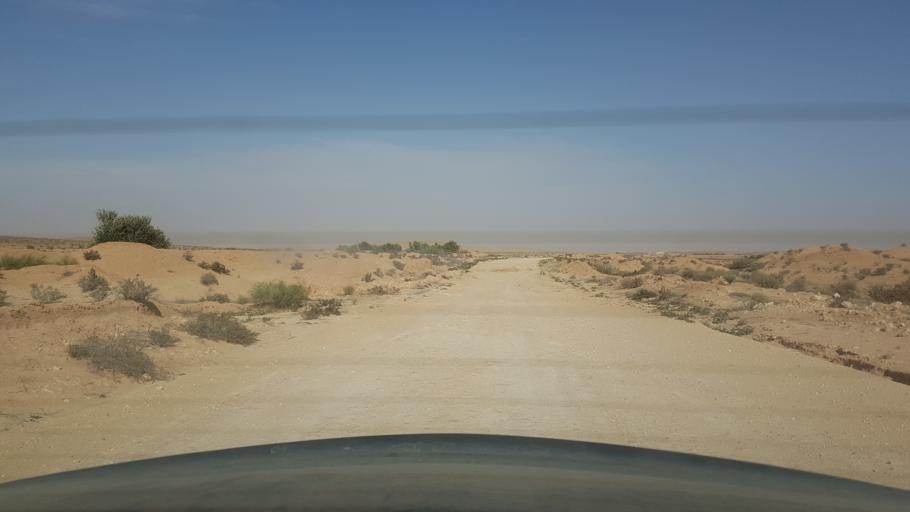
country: TN
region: Qabis
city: El Hamma
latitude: 33.6625
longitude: 9.7351
